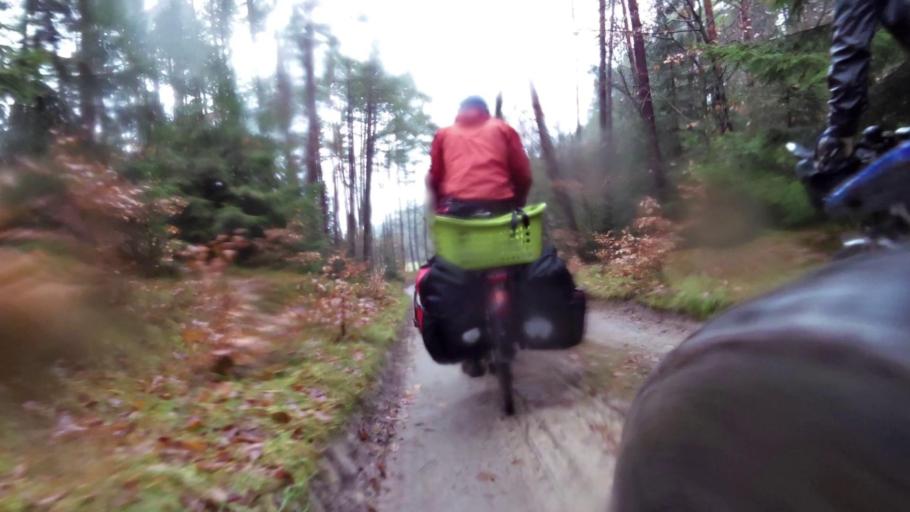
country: PL
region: West Pomeranian Voivodeship
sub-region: Powiat drawski
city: Zlocieniec
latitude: 53.5589
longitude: 15.9283
